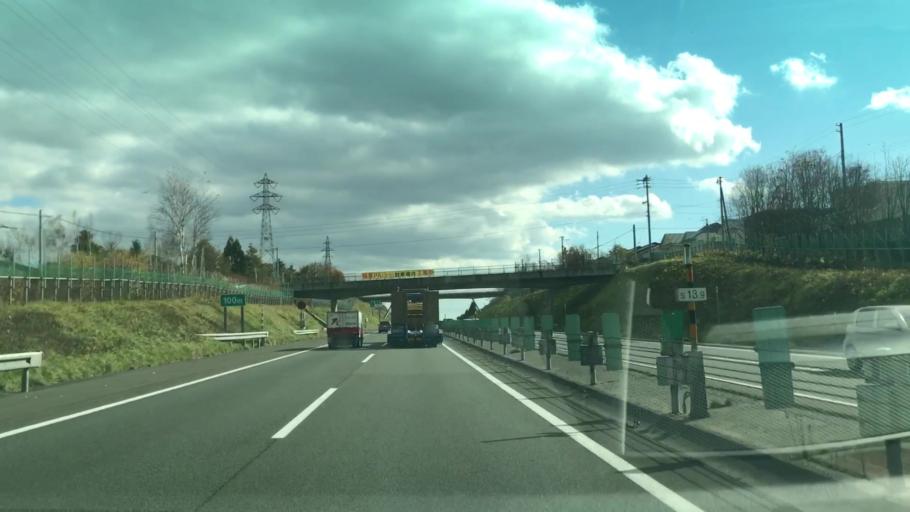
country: JP
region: Hokkaido
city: Kitahiroshima
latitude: 42.9673
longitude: 141.4918
